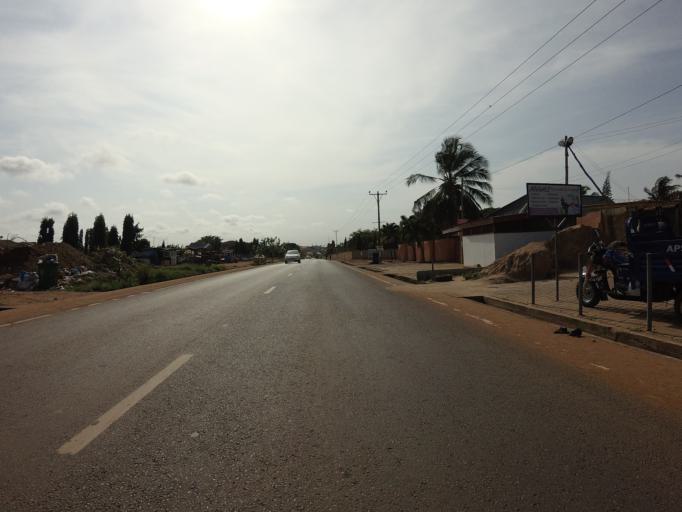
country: GH
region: Greater Accra
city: Nungua
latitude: 5.6450
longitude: -0.0971
